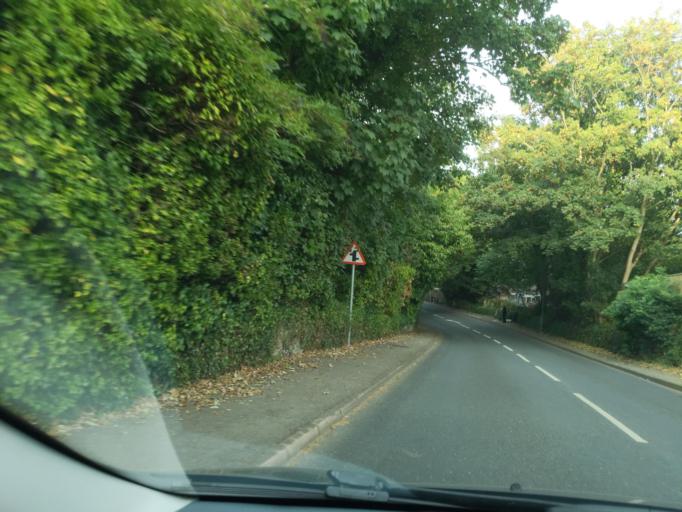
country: GB
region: England
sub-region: Cornwall
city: Torpoint
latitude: 50.3737
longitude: -4.2150
